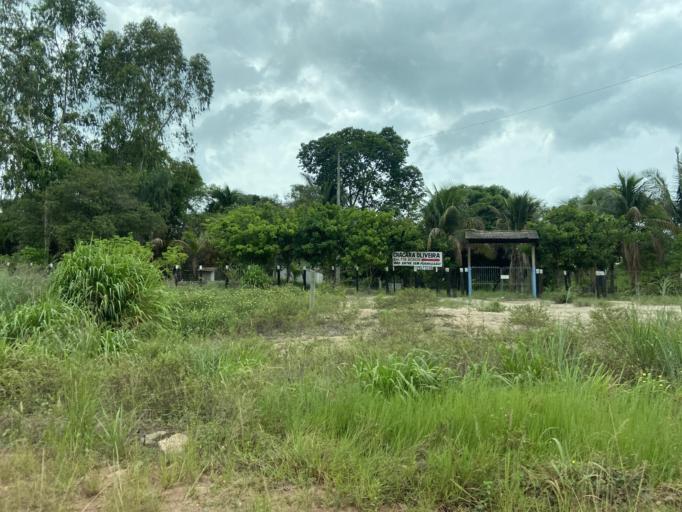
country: BR
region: Para
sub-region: Maraba
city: Maraba
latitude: -5.2731
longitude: -49.0206
